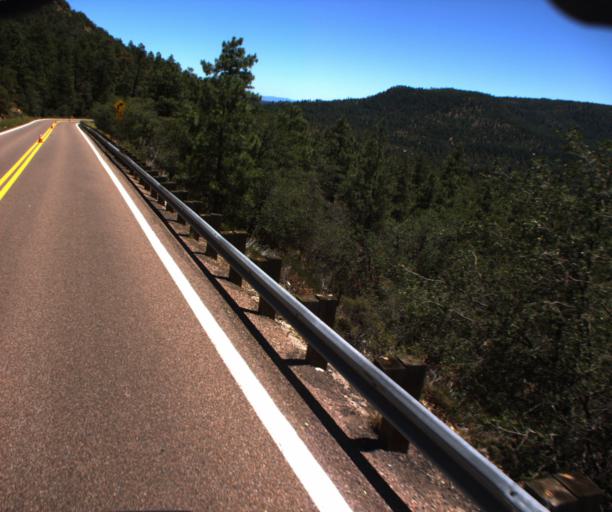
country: US
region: Arizona
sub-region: Gila County
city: Pine
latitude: 34.4177
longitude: -111.5001
